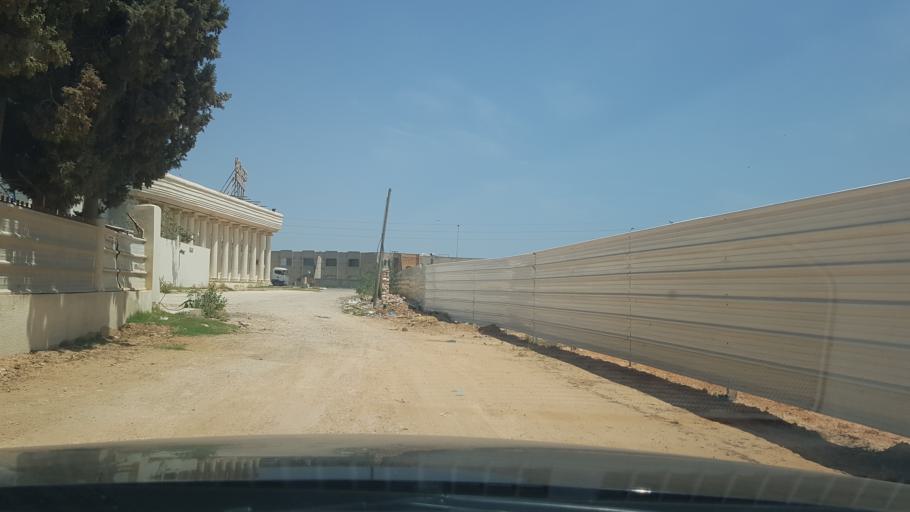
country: TN
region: Safaqis
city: Al Qarmadah
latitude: 34.8427
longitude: 10.7617
